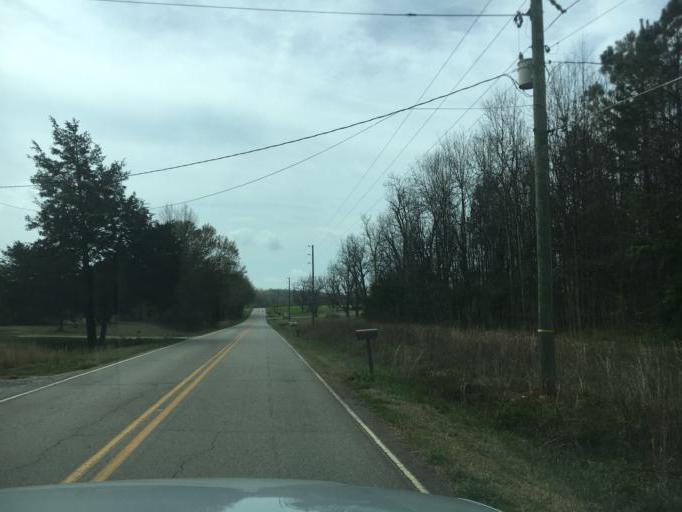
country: US
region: Georgia
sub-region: Hart County
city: Royston
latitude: 34.3500
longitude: -83.0412
